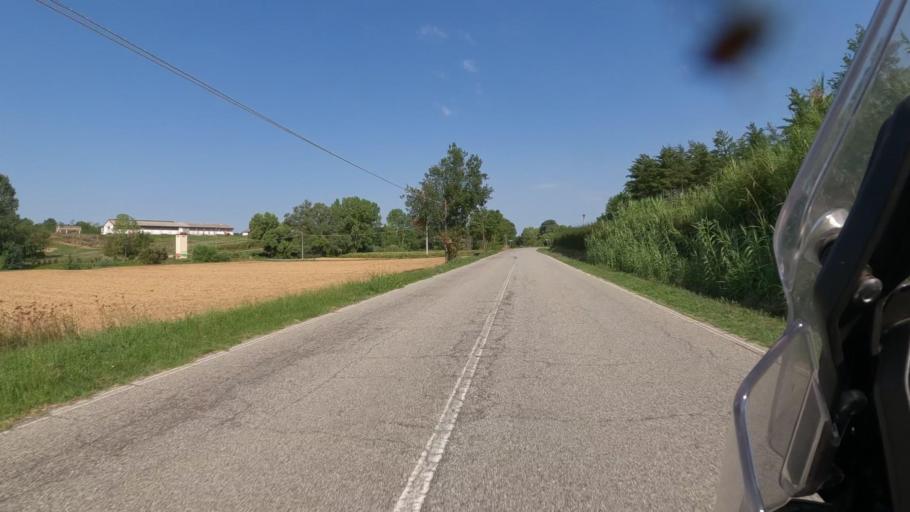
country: IT
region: Piedmont
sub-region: Provincia di Alessandria
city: Quattordio
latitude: 44.9110
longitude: 8.3974
